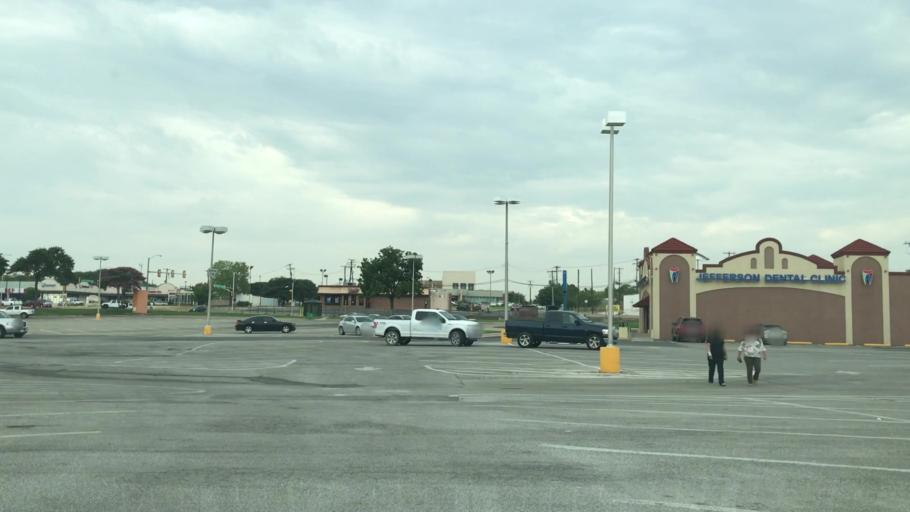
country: US
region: Texas
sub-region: Tarrant County
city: Edgecliff Village
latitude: 32.6862
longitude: -97.3282
